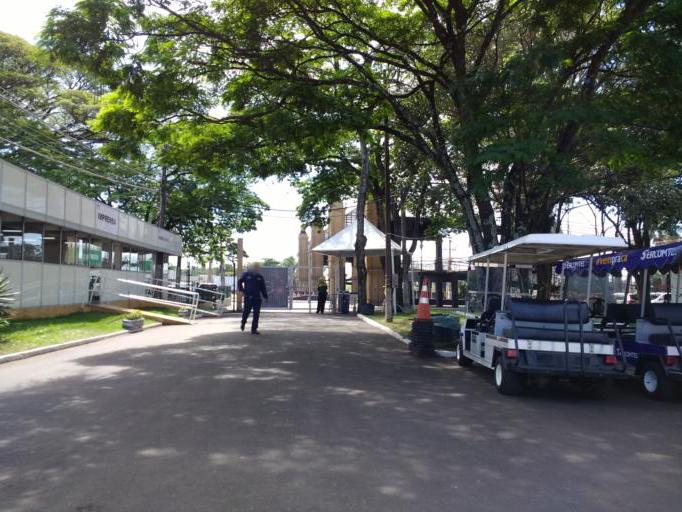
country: BR
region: Parana
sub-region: Cambe
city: Cambe
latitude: -23.2886
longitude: -51.2258
